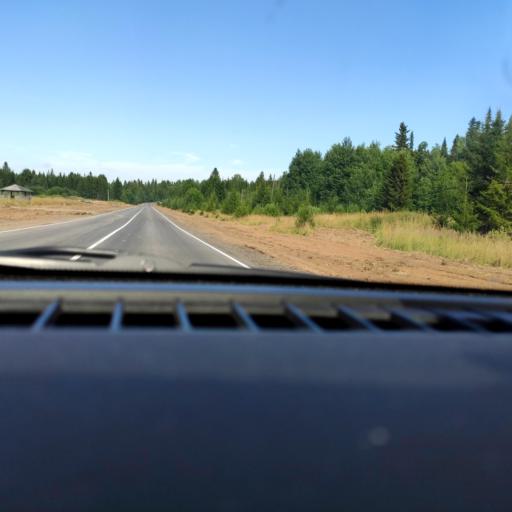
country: RU
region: Perm
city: Polazna
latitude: 58.3384
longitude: 56.2129
